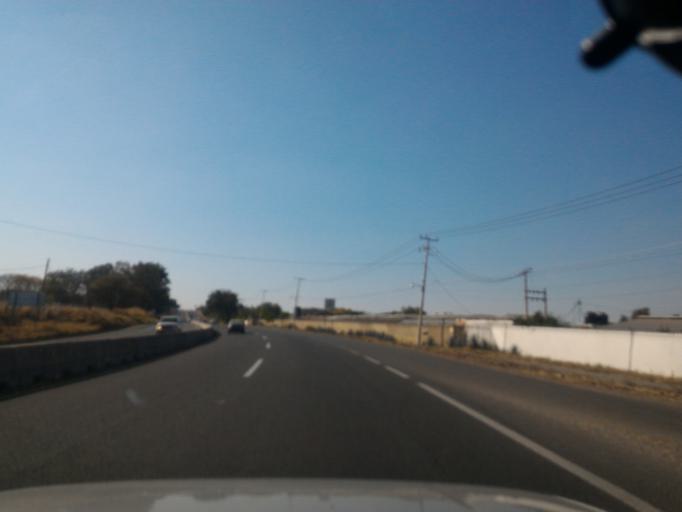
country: MX
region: Jalisco
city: Atequiza
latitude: 20.3984
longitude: -103.1496
